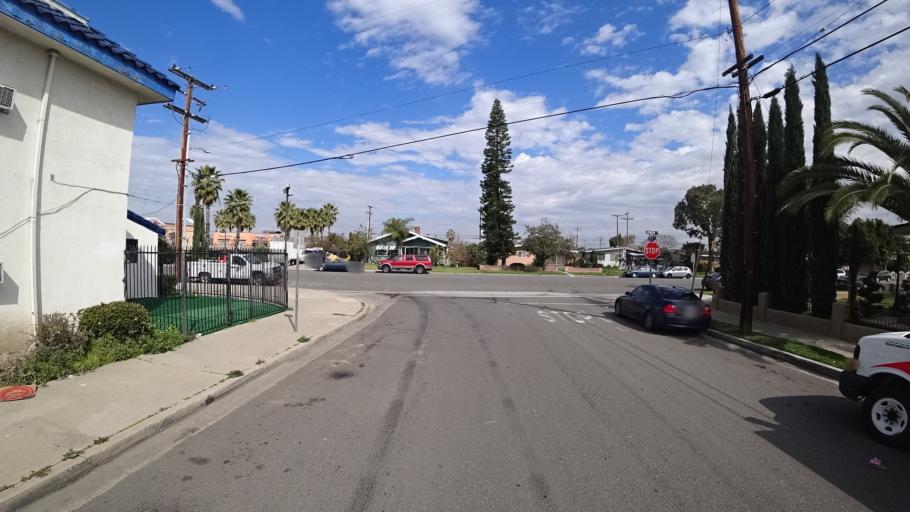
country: US
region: California
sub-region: Orange County
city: Anaheim
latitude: 33.8410
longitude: -117.8882
